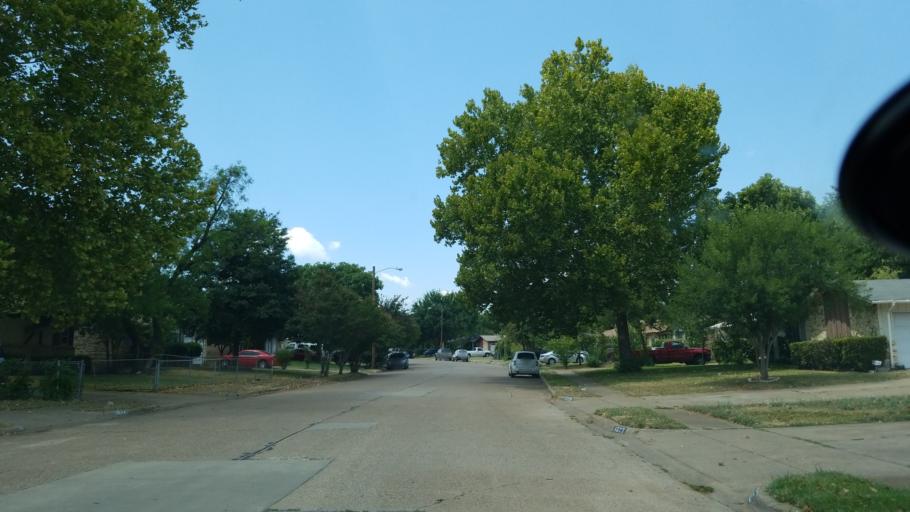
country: US
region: Texas
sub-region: Dallas County
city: Cockrell Hill
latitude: 32.7136
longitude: -96.8969
